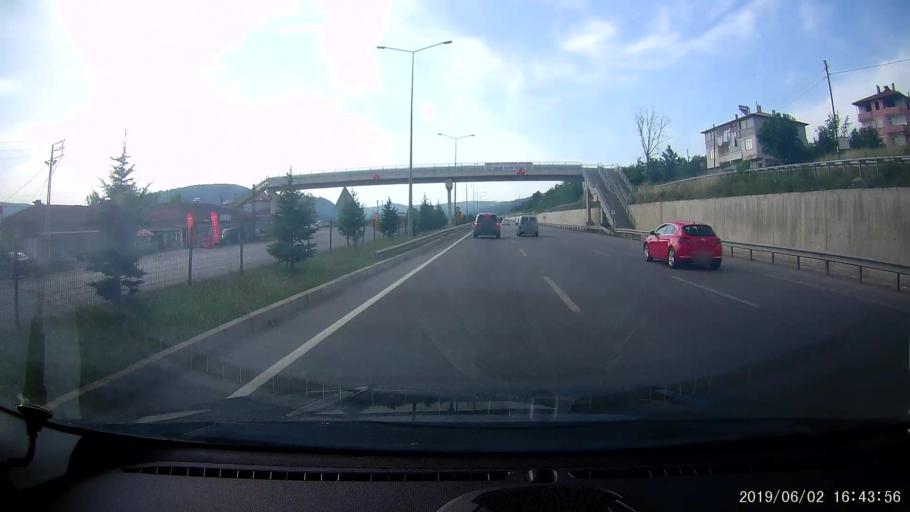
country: TR
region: Samsun
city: Kavak
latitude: 41.1430
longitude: 36.1182
